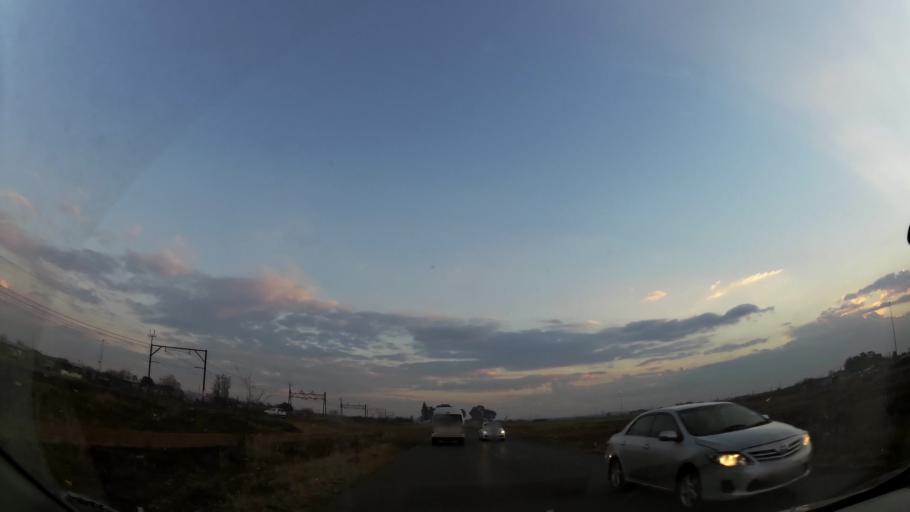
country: ZA
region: Gauteng
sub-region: City of Johannesburg Metropolitan Municipality
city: Orange Farm
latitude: -26.5519
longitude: 27.8827
